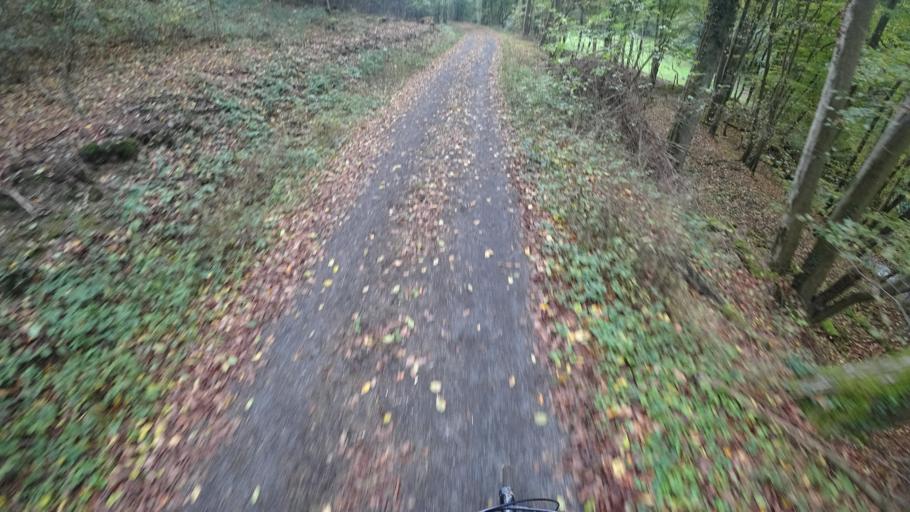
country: DE
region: Rheinland-Pfalz
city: Isselbach
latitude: 50.3936
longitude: 7.8926
